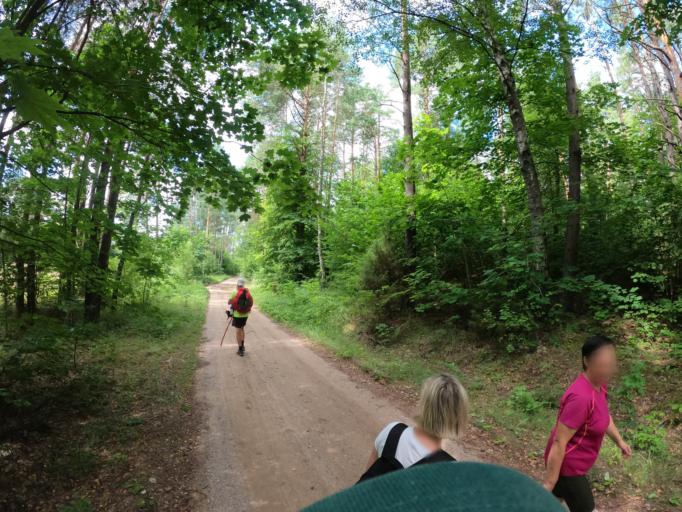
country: LT
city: Jieznas
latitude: 54.6582
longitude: 24.1159
